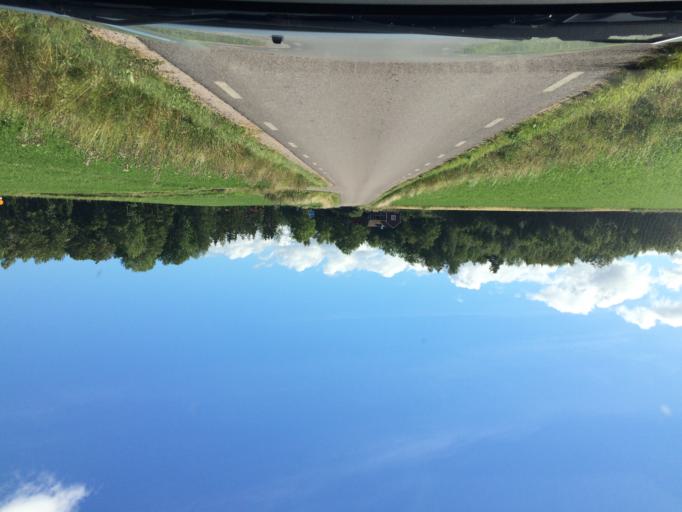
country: SE
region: Soedermanland
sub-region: Eskilstuna Kommun
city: Kvicksund
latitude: 59.5046
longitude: 16.3743
